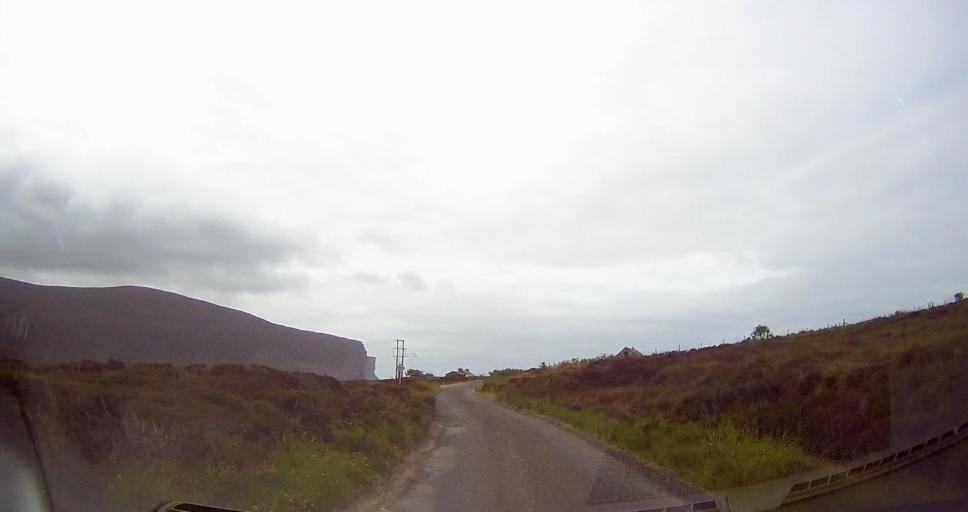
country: GB
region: Scotland
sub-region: Orkney Islands
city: Stromness
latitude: 58.8780
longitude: -3.3860
